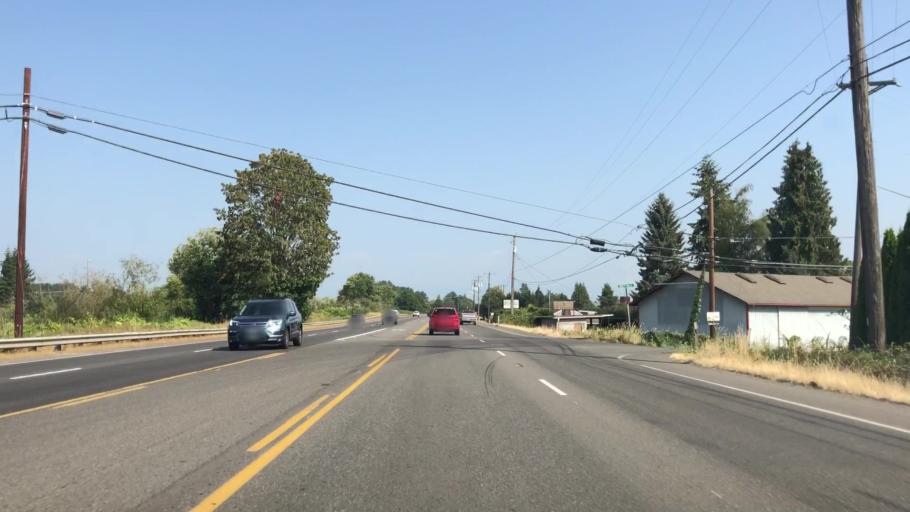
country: US
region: Washington
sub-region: Pierce County
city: Fife
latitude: 47.2242
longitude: -122.3628
